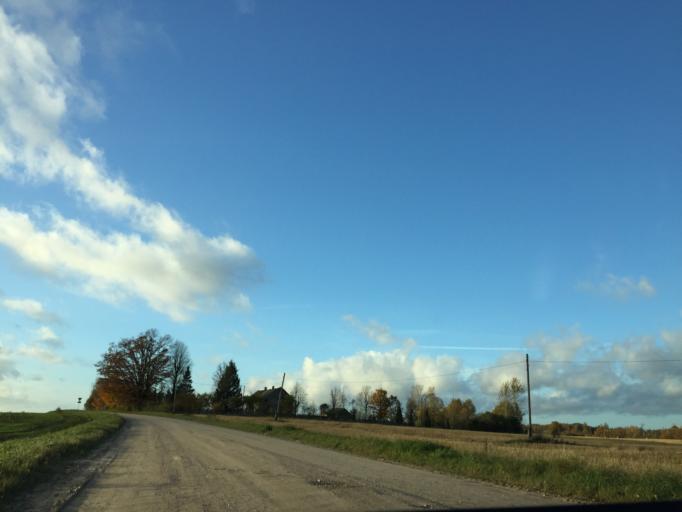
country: LV
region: Ogre
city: Jumprava
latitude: 56.7965
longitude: 25.0446
